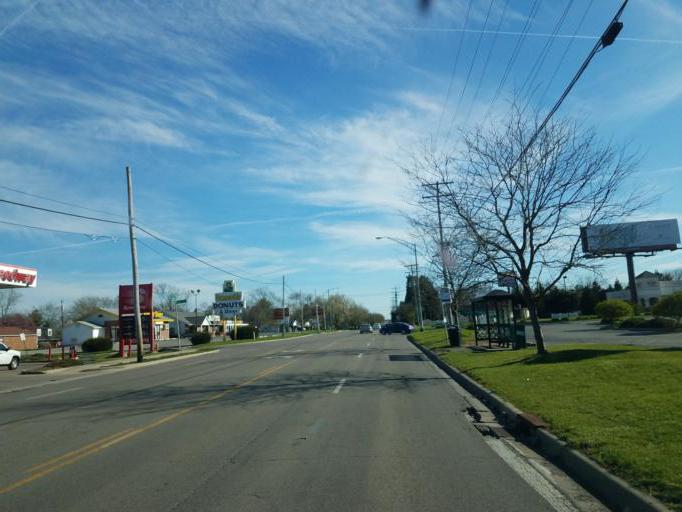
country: US
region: Ohio
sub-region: Franklin County
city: Worthington
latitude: 40.0508
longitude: -83.0498
